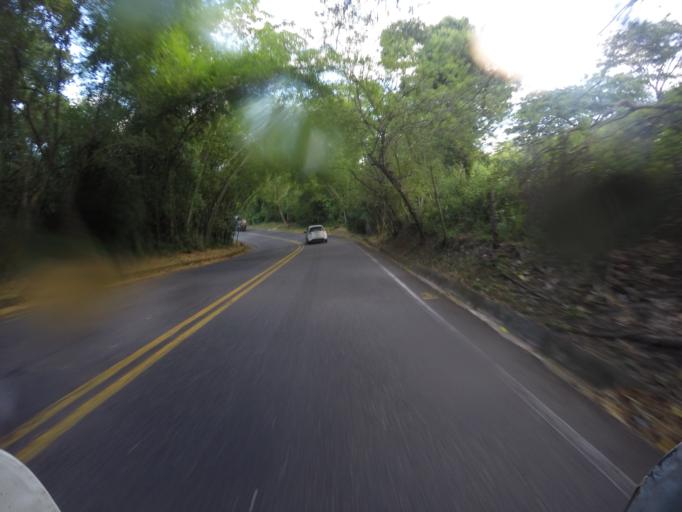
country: CO
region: Valle del Cauca
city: Cartago
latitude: 4.7290
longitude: -75.8685
